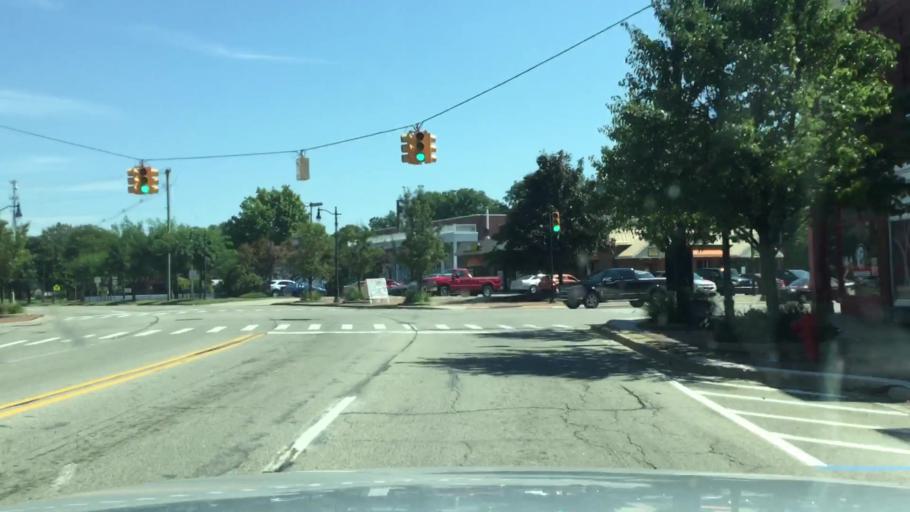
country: US
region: Michigan
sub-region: Lenawee County
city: Clinton
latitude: 42.0720
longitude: -83.9721
